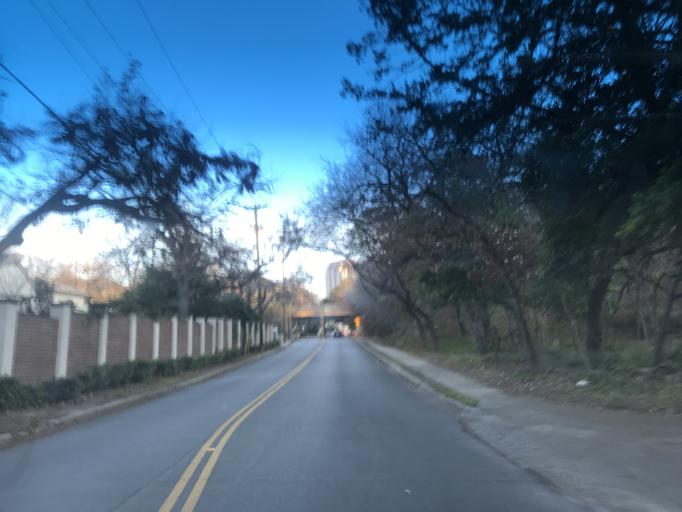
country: US
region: Texas
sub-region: Dallas County
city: Highland Park
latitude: 32.8125
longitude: -96.8002
